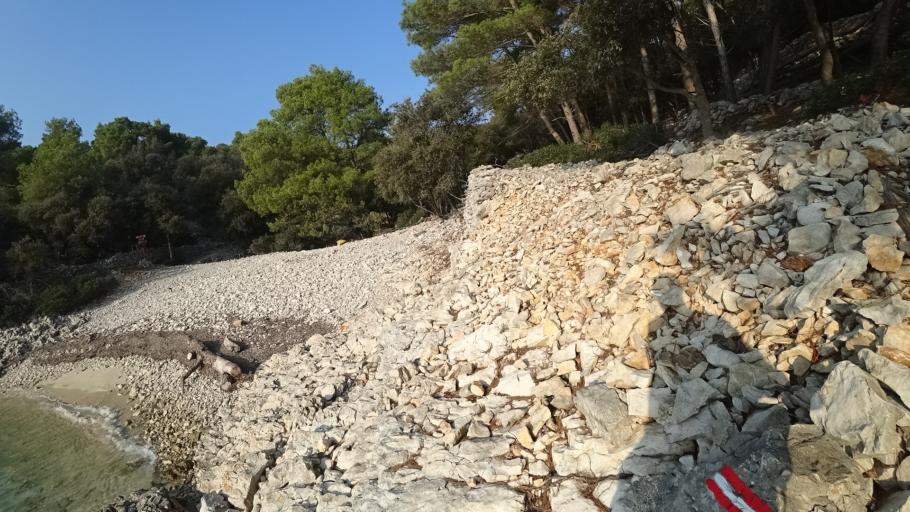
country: HR
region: Primorsko-Goranska
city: Mali Losinj
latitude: 44.5137
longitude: 14.4754
